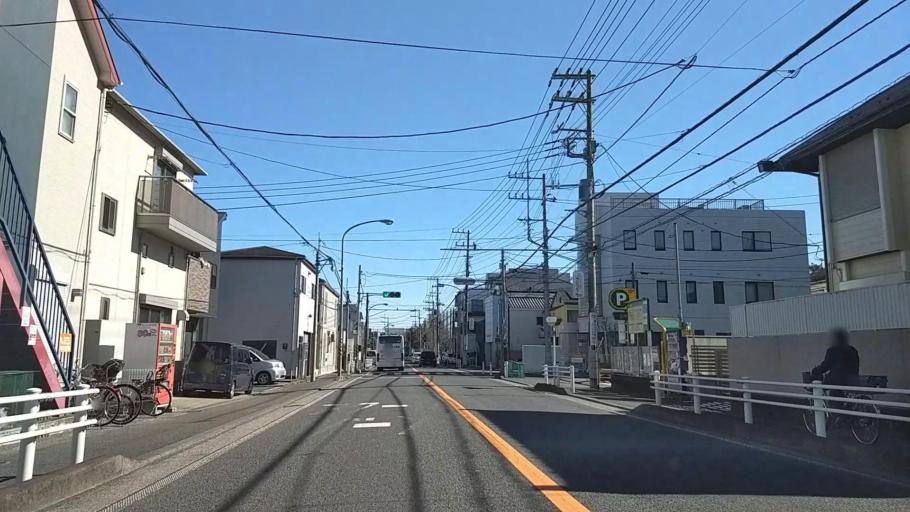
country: JP
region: Kanagawa
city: Zushi
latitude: 35.3279
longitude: 139.6090
